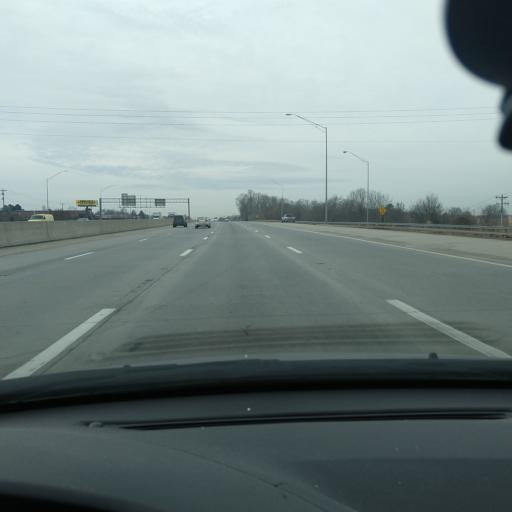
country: US
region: North Carolina
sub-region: Rowan County
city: Salisbury
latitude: 35.6563
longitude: -80.4620
